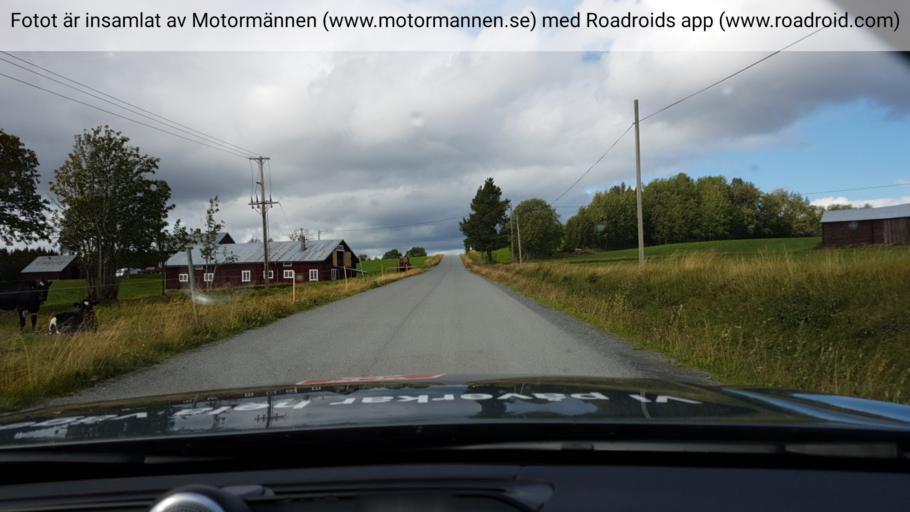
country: SE
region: Jaemtland
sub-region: OEstersunds Kommun
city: Lit
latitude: 63.6391
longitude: 14.9598
